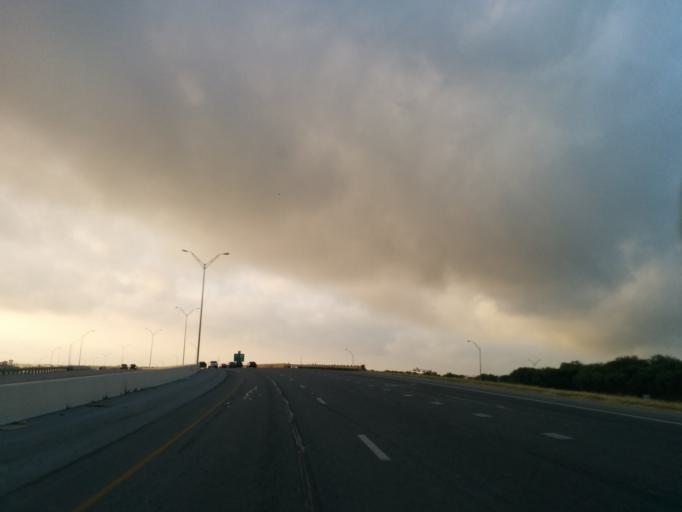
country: US
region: Texas
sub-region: Bexar County
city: Lackland Air Force Base
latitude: 29.4396
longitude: -98.6602
